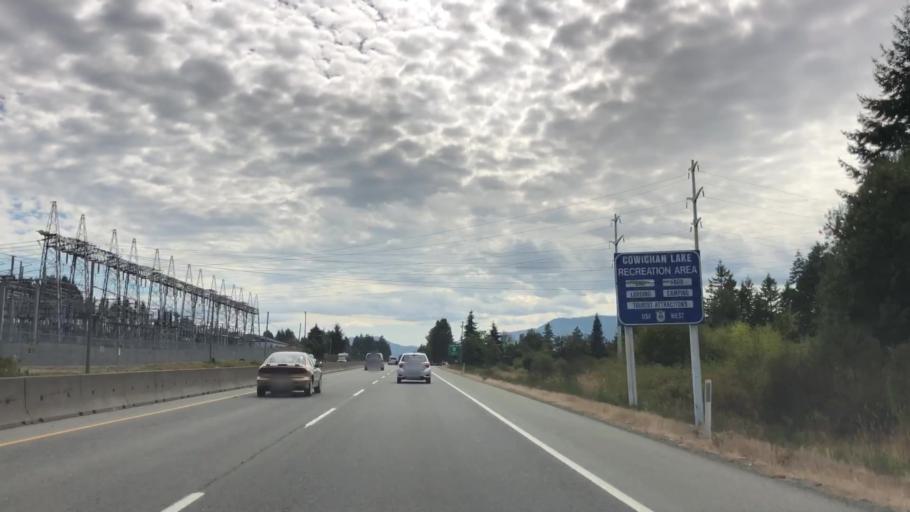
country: CA
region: British Columbia
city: North Cowichan
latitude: 48.8274
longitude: -123.7181
